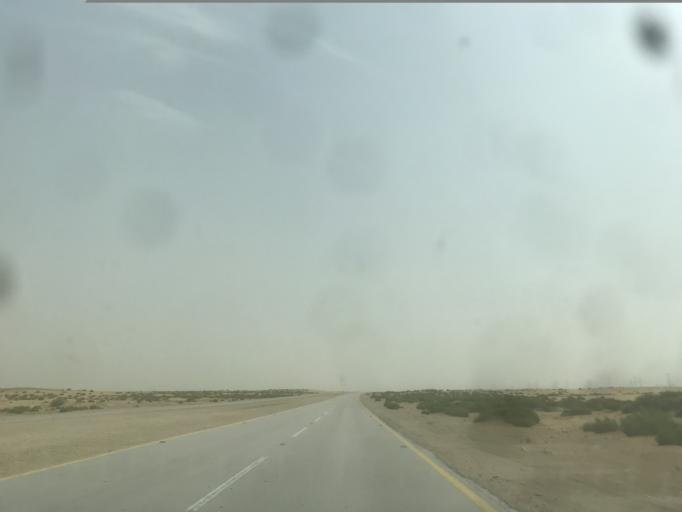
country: SA
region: Eastern Province
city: Abqaiq
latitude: 25.9173
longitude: 49.8559
